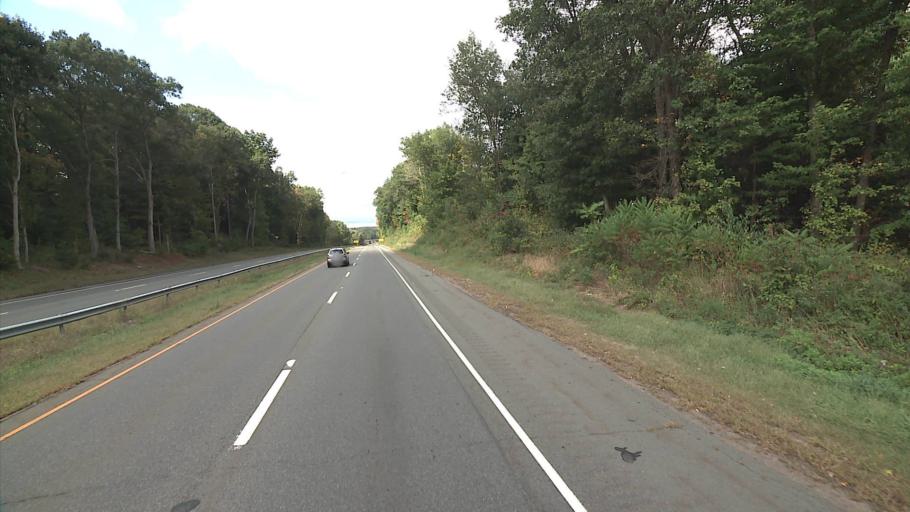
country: US
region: Connecticut
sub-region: New Haven County
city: Meriden
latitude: 41.5518
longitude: -72.7740
